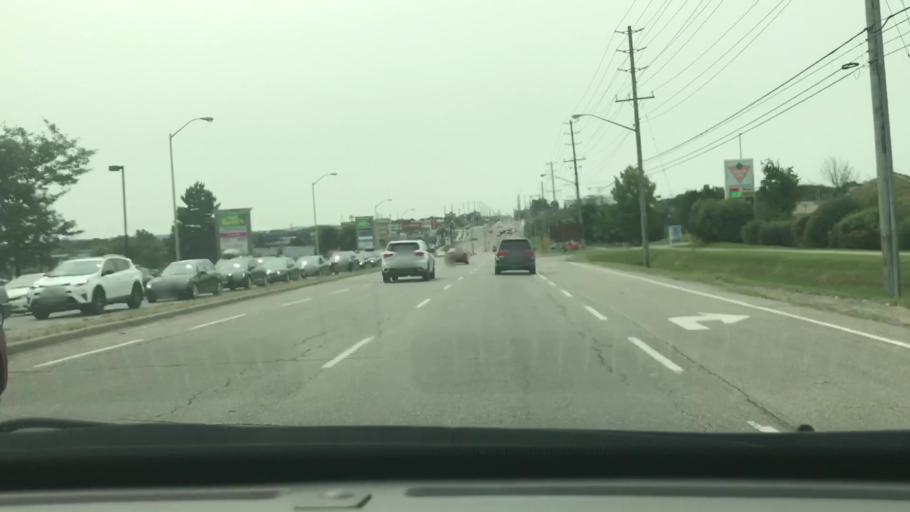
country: CA
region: Ontario
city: Newmarket
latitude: 44.0604
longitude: -79.4818
